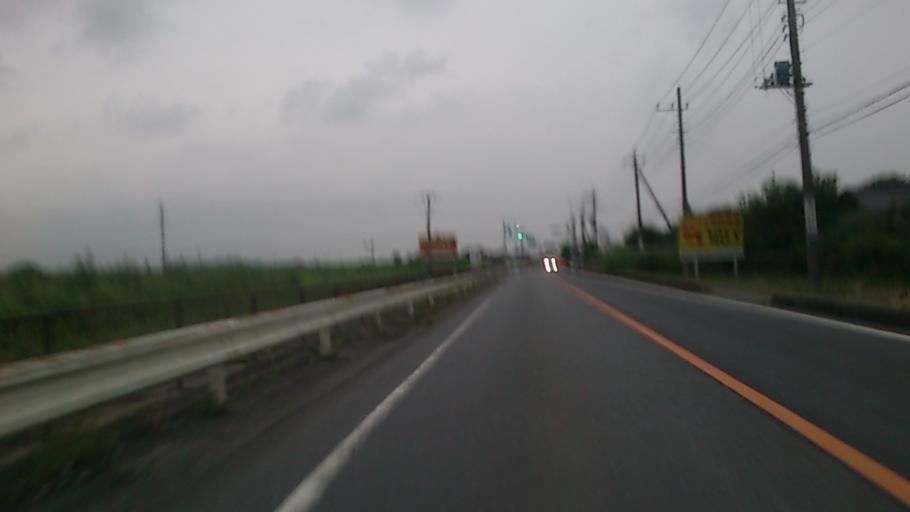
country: JP
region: Saitama
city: Kazo
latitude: 36.1649
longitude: 139.5880
